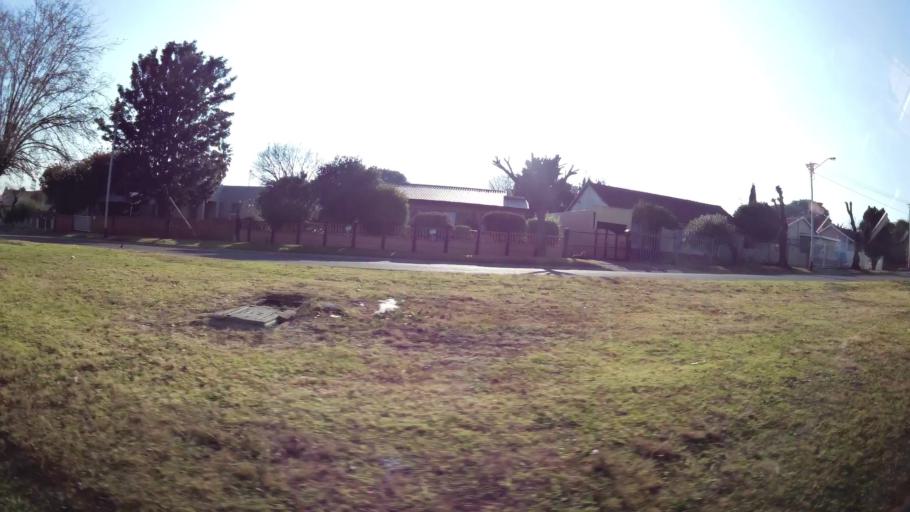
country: ZA
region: Gauteng
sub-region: City of Johannesburg Metropolitan Municipality
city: Modderfontein
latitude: -26.1451
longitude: 28.1944
